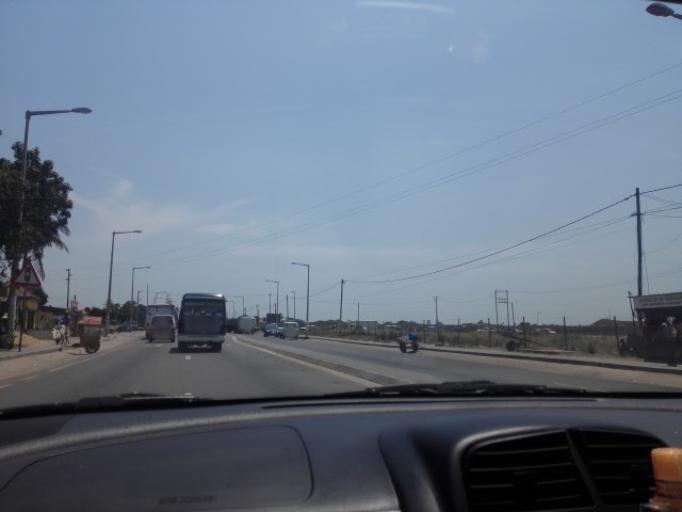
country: MZ
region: Maputo City
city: Maputo
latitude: -25.9228
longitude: 32.5612
